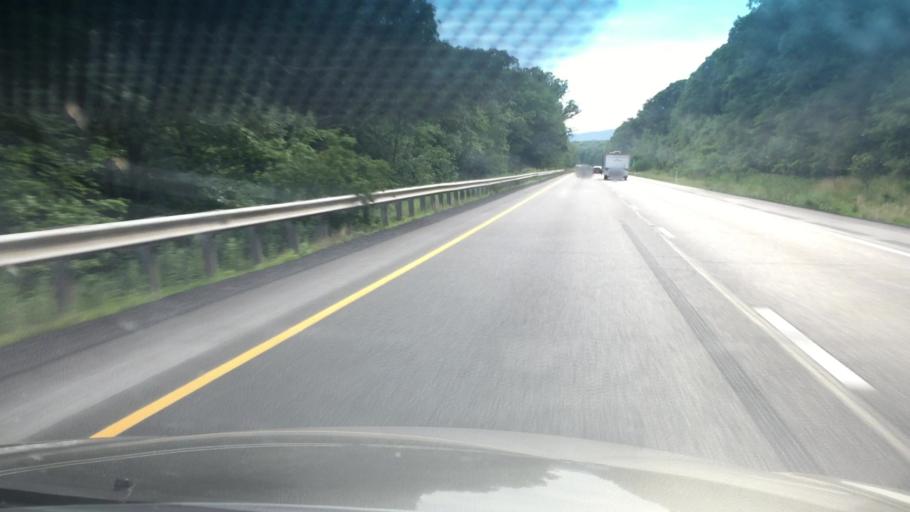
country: US
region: Pennsylvania
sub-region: Luzerne County
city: Freeland
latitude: 41.0615
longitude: -75.8866
